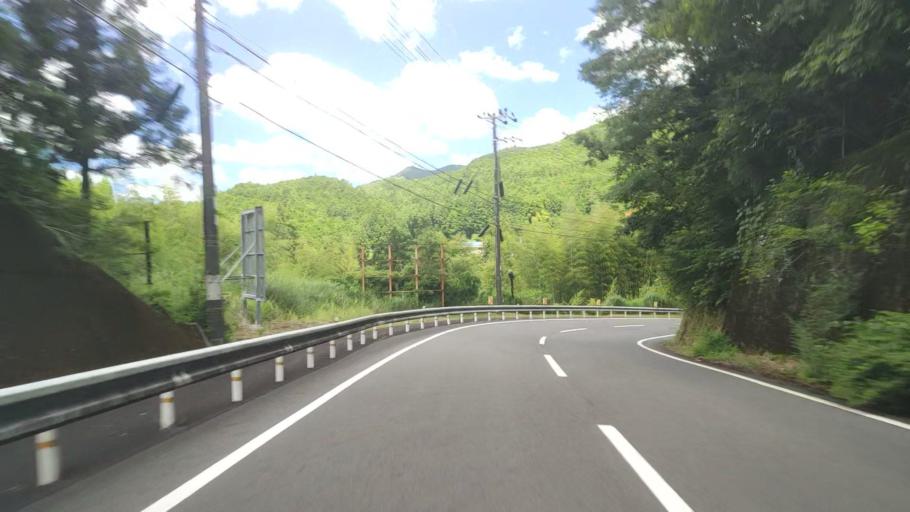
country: JP
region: Mie
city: Owase
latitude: 33.9556
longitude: 136.0690
